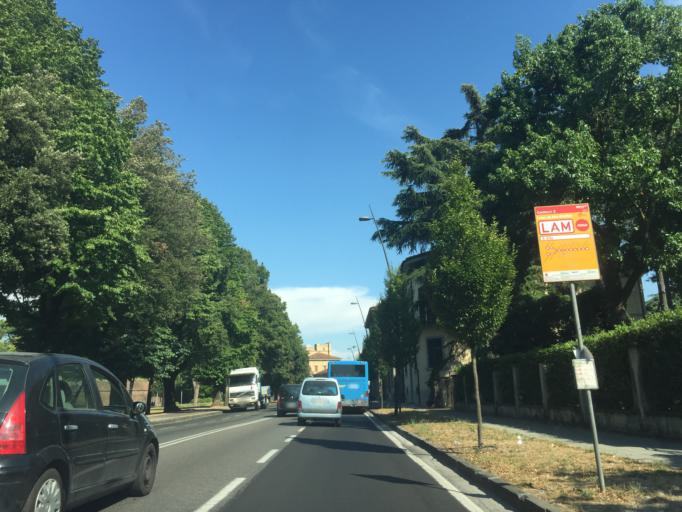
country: IT
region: Tuscany
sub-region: Provincia di Lucca
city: Lucca
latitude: 43.8386
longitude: 10.4986
